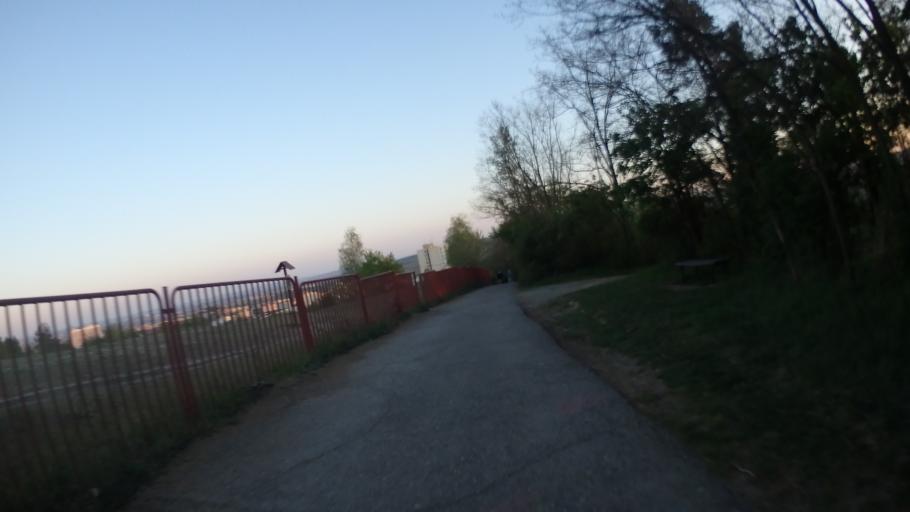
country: CZ
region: South Moravian
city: Ostopovice
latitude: 49.1812
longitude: 16.5545
